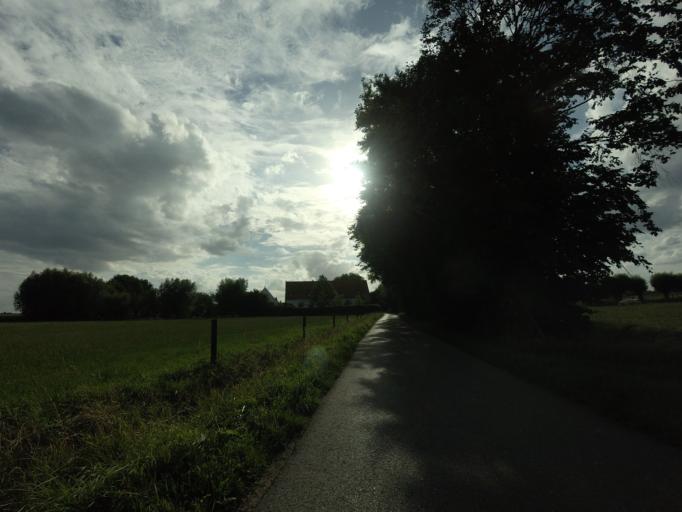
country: BE
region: Flanders
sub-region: Provincie Vlaams-Brabant
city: Grimbergen
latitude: 50.9545
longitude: 4.3990
